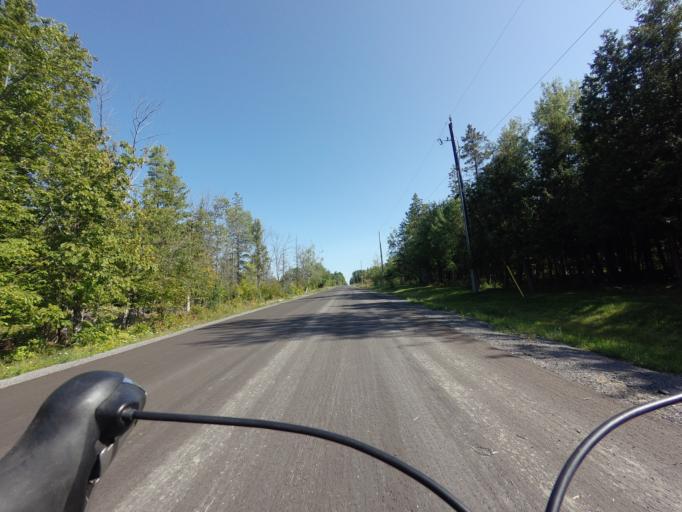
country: CA
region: Ontario
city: Bells Corners
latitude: 45.4670
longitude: -75.9852
